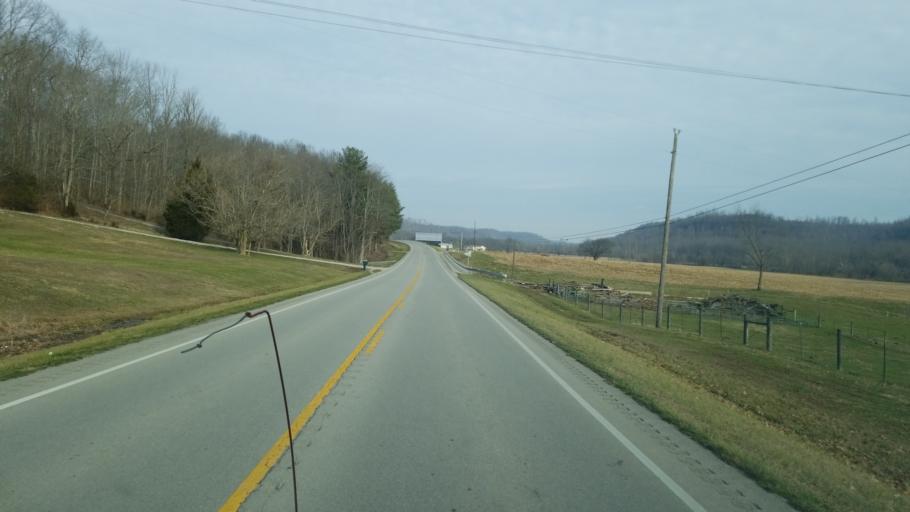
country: US
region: Kentucky
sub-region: Casey County
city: Liberty
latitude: 37.3637
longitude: -84.8674
